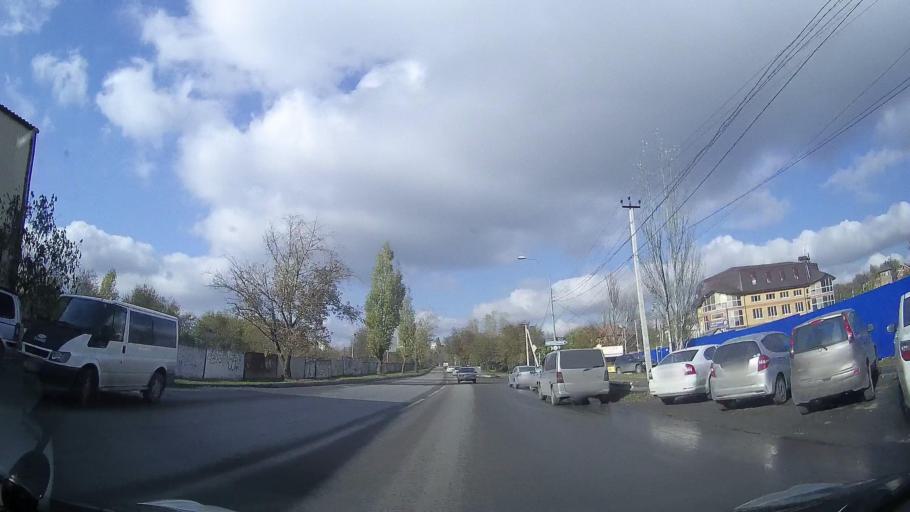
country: RU
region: Rostov
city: Rostov-na-Donu
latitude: 47.2248
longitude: 39.6850
